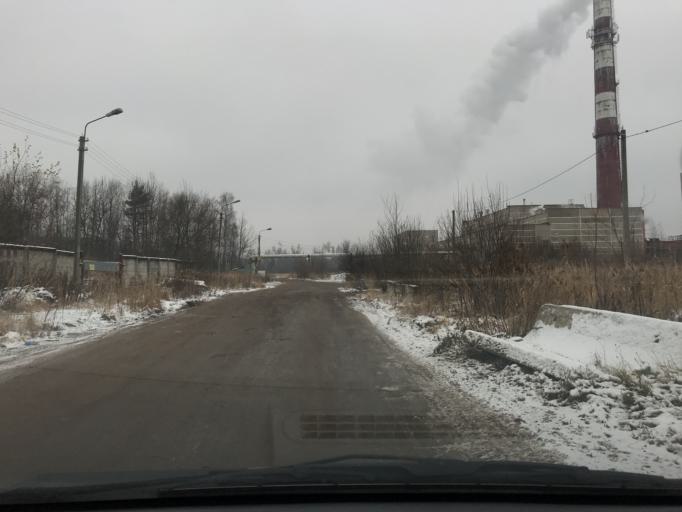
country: RU
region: Moskovskaya
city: Elektrostal'
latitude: 55.8142
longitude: 38.4392
